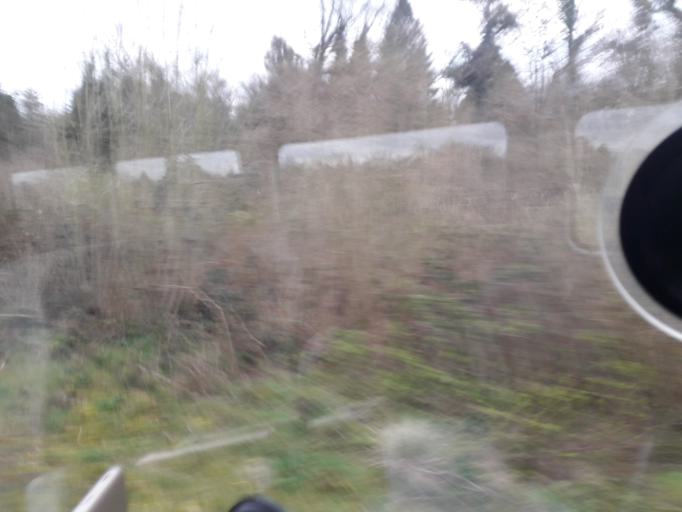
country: IE
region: Leinster
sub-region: An Iarmhi
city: An Muileann gCearr
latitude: 53.5923
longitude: -7.3883
